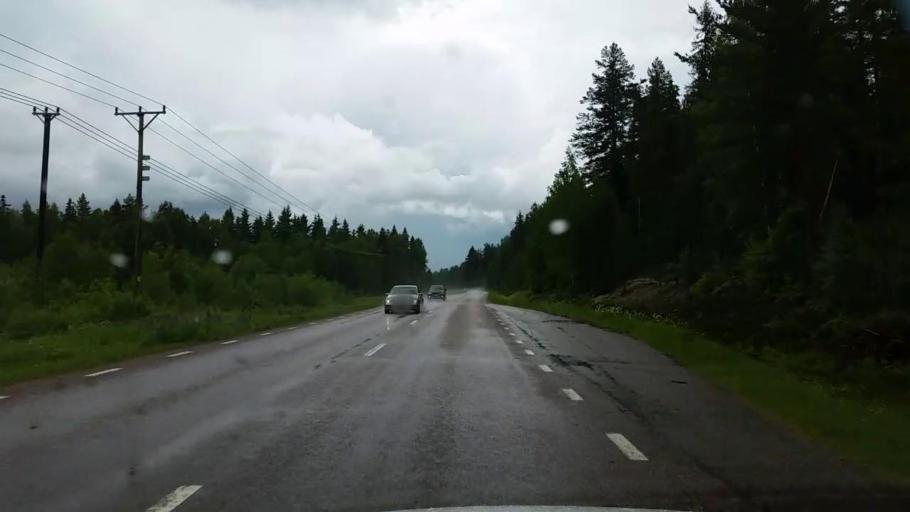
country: SE
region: Gaevleborg
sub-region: Sandvikens Kommun
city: Jarbo
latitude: 60.6774
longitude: 16.6162
